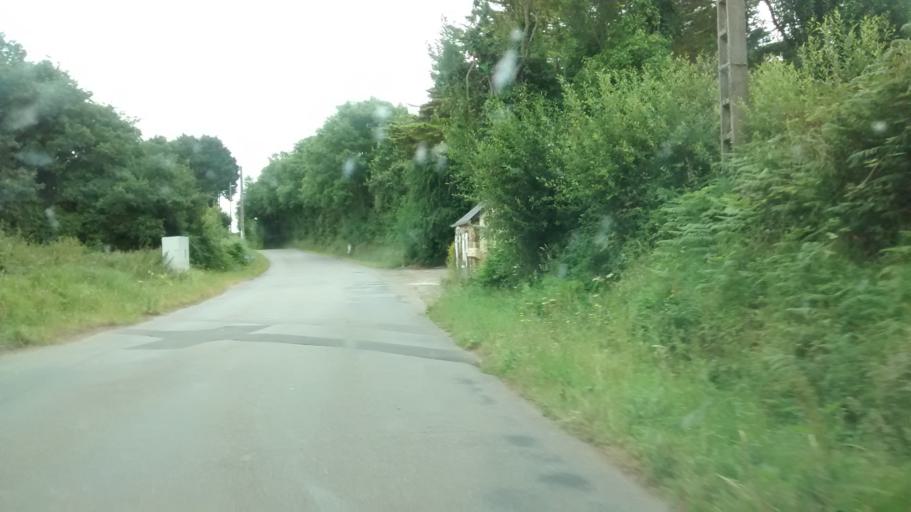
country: FR
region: Brittany
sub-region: Departement du Finistere
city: Plougastel-Daoulas
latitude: 48.3503
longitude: -4.3907
